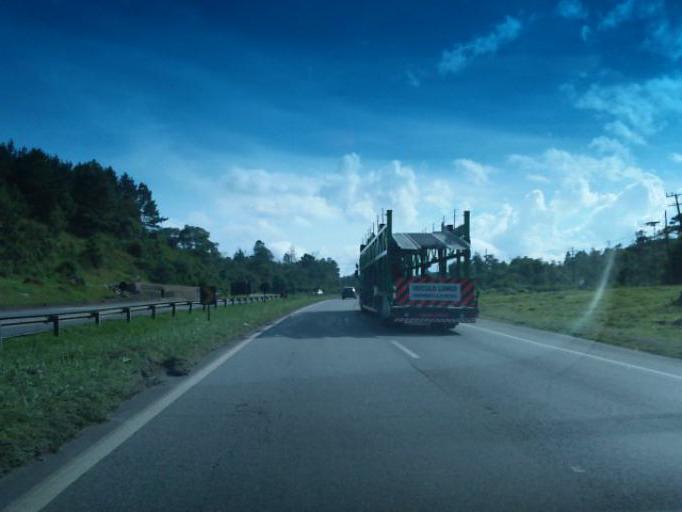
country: BR
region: Parana
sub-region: Campina Grande Do Sul
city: Campina Grande do Sul
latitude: -25.2927
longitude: -48.9347
